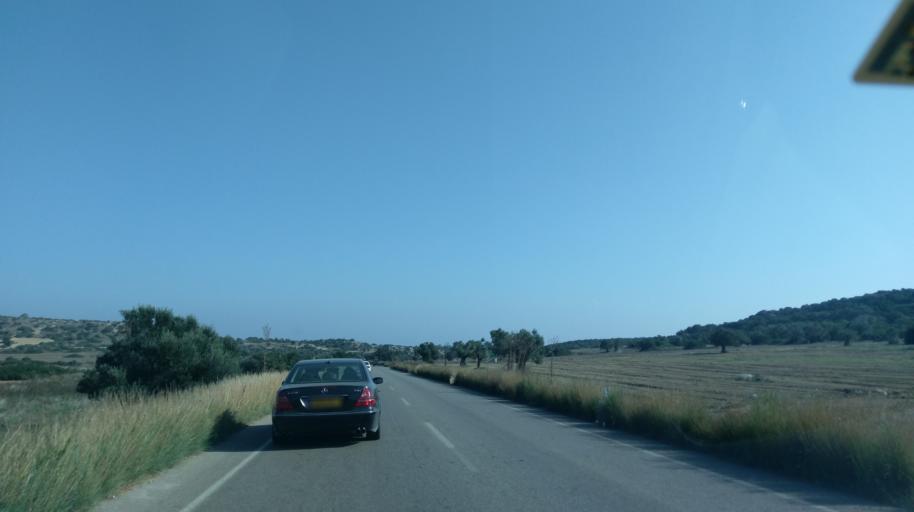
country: CY
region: Ammochostos
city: Leonarisso
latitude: 35.4014
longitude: 34.0919
